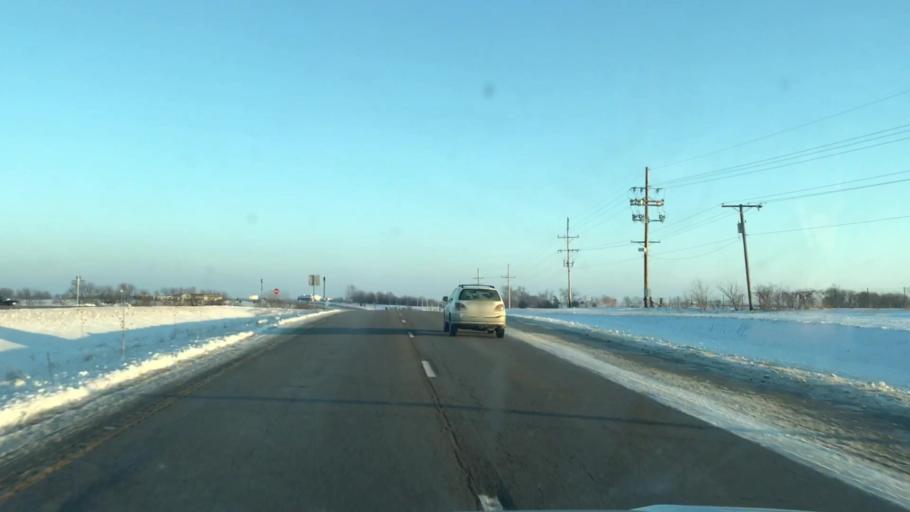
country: US
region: Missouri
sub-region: Clinton County
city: Cameron
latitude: 39.7594
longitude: -94.3477
